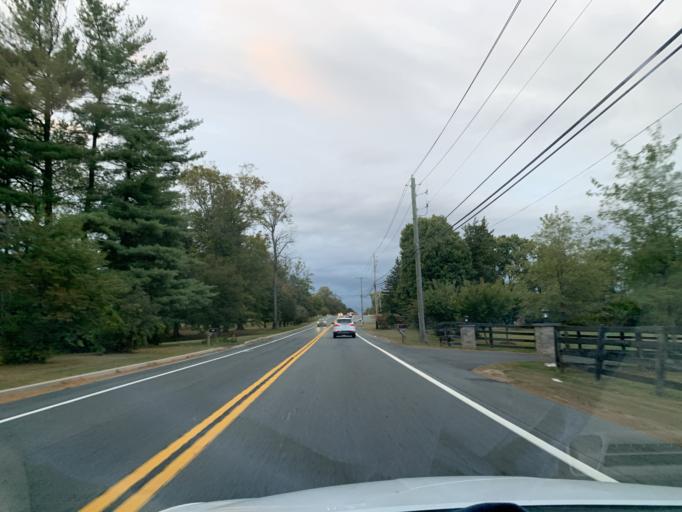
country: US
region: Maryland
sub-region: Harford County
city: Riverside
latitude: 39.4975
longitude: -76.2629
